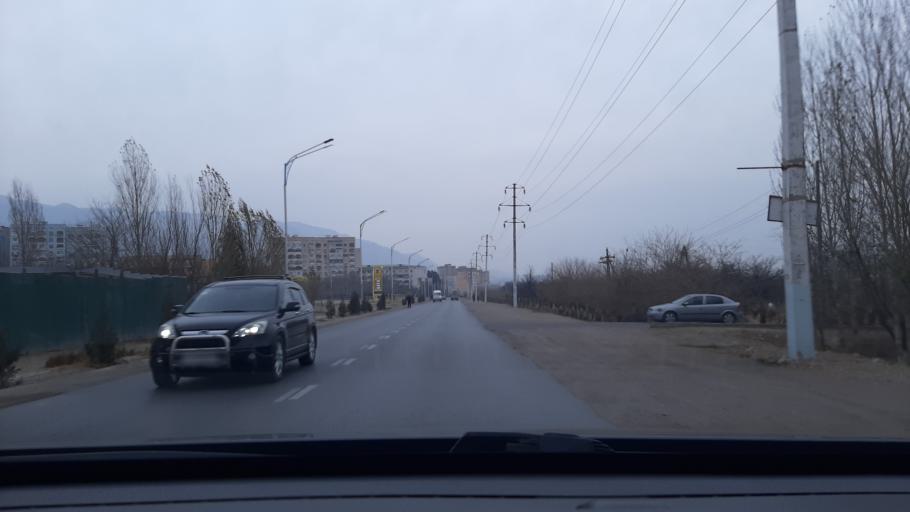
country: TJ
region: Viloyati Sughd
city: Khujand
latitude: 40.2830
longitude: 69.5874
